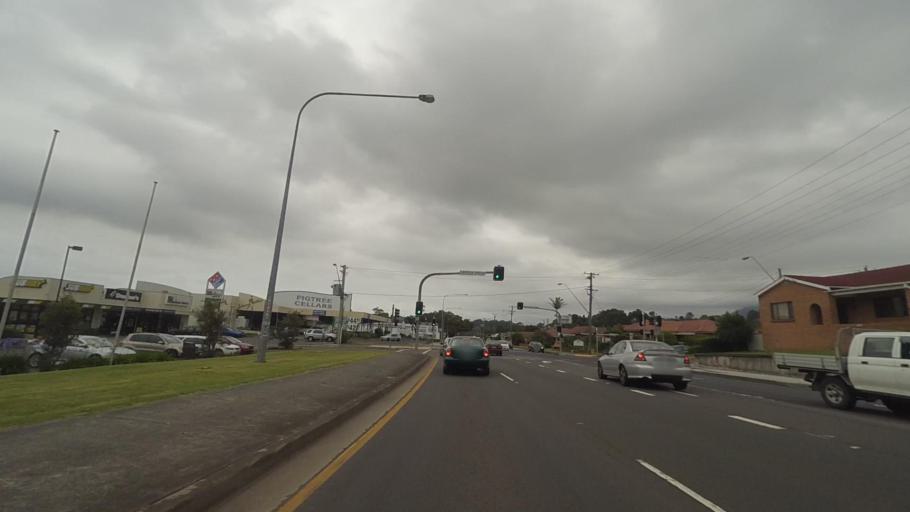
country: AU
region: New South Wales
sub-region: Wollongong
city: West Wollongong
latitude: -34.4318
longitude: 150.8658
